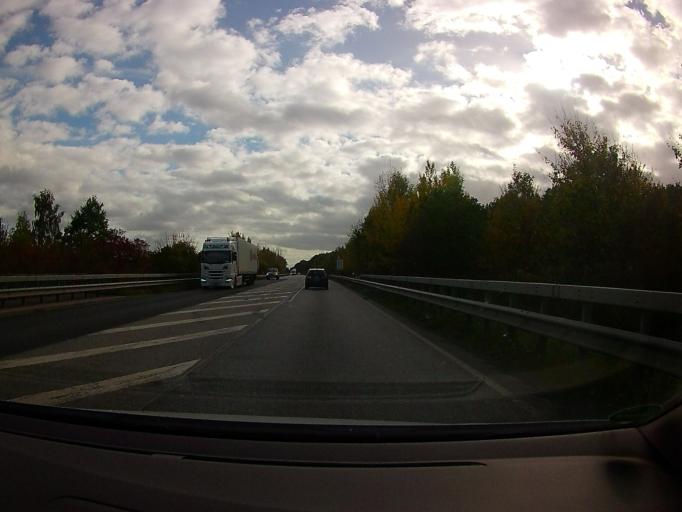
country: DE
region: Schleswig-Holstein
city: Kasseburg
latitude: 53.5735
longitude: 10.4007
